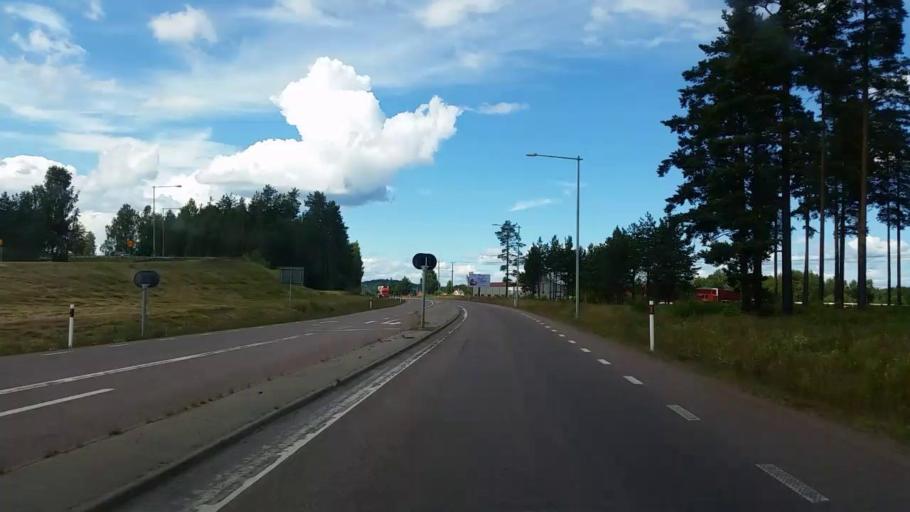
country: SE
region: Dalarna
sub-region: Leksand Municipality
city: Leksand
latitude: 60.7194
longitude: 15.0233
